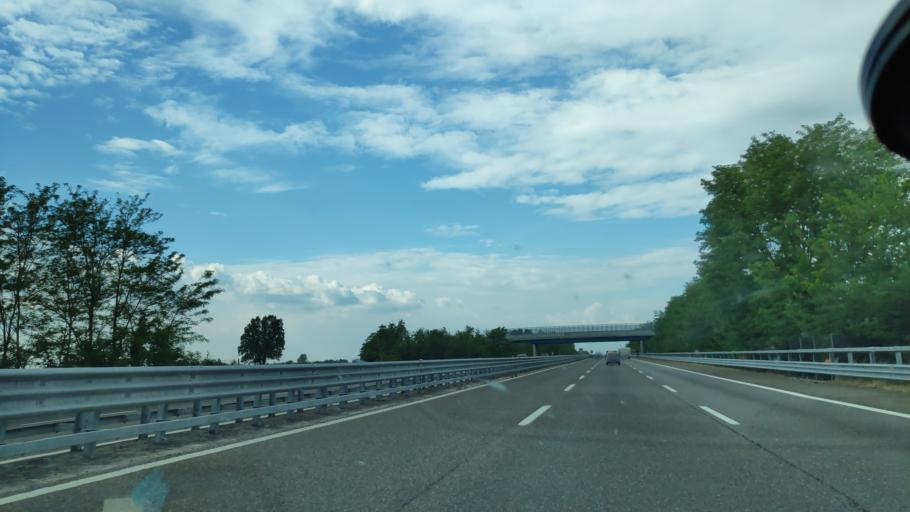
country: IT
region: Lombardy
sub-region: Provincia di Pavia
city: Gropello Cairoli
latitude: 45.1554
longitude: 8.9953
